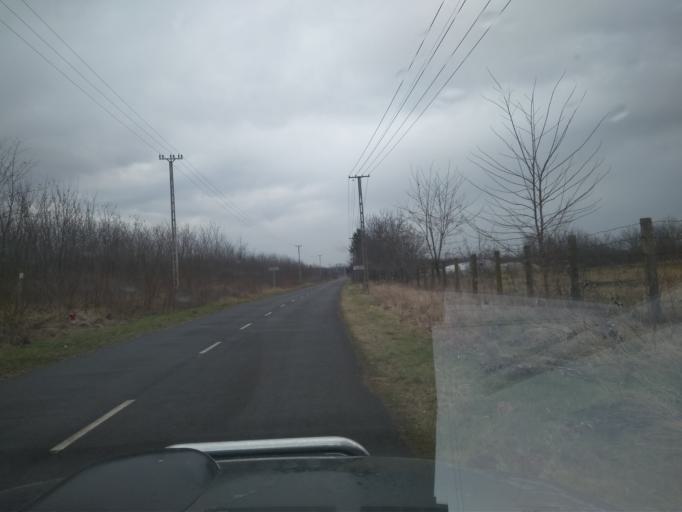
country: HU
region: Szabolcs-Szatmar-Bereg
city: Nyirpazony
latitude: 48.0287
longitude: 21.7834
